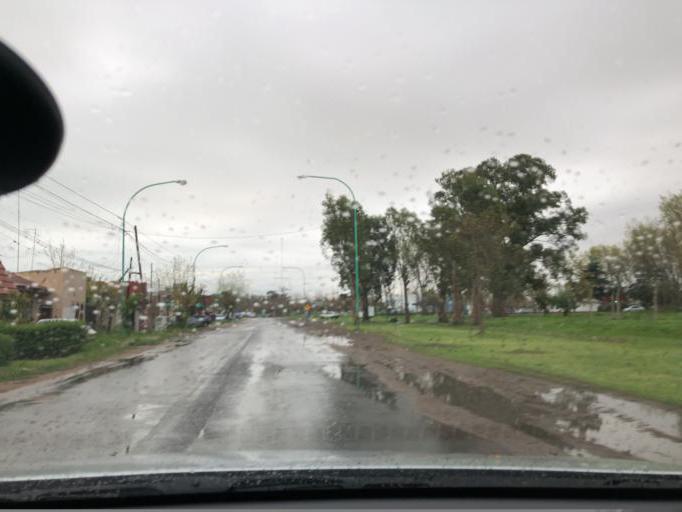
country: AR
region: Buenos Aires
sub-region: Partido de Ensenada
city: Ensenada
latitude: -34.8351
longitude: -57.9463
